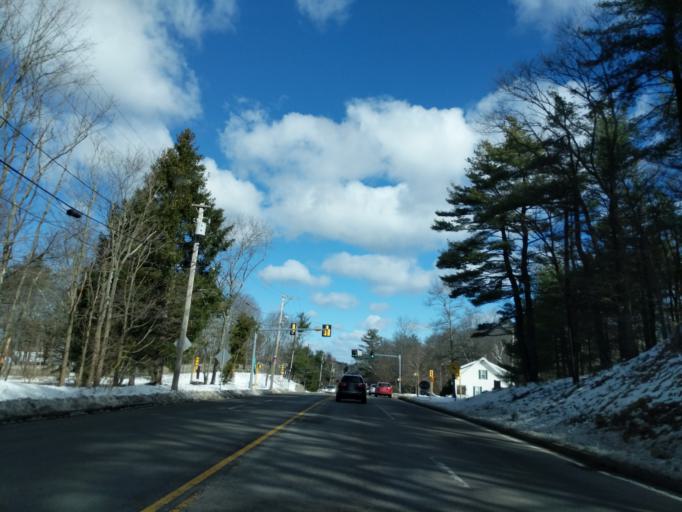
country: US
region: Massachusetts
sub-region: Norfolk County
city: Milton
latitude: 42.2236
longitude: -71.0706
